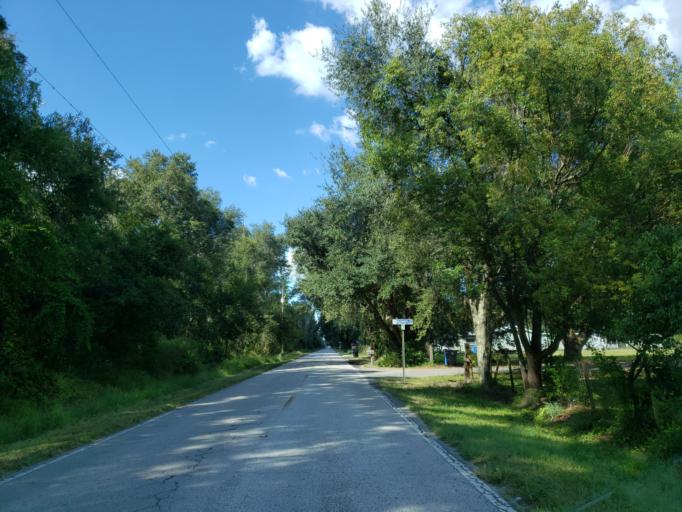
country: US
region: Florida
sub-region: Hillsborough County
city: Valrico
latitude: 27.9422
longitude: -82.2030
